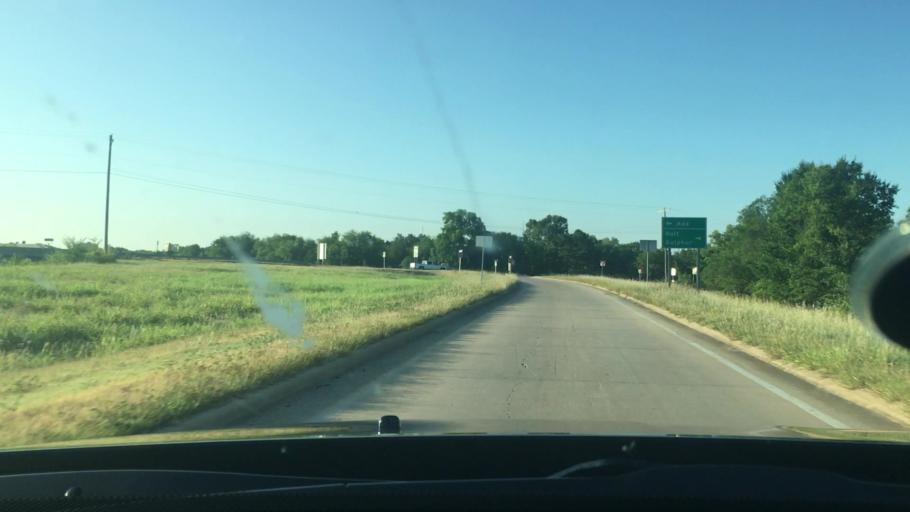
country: US
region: Oklahoma
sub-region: Pontotoc County
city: Ada
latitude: 34.7643
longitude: -96.7032
